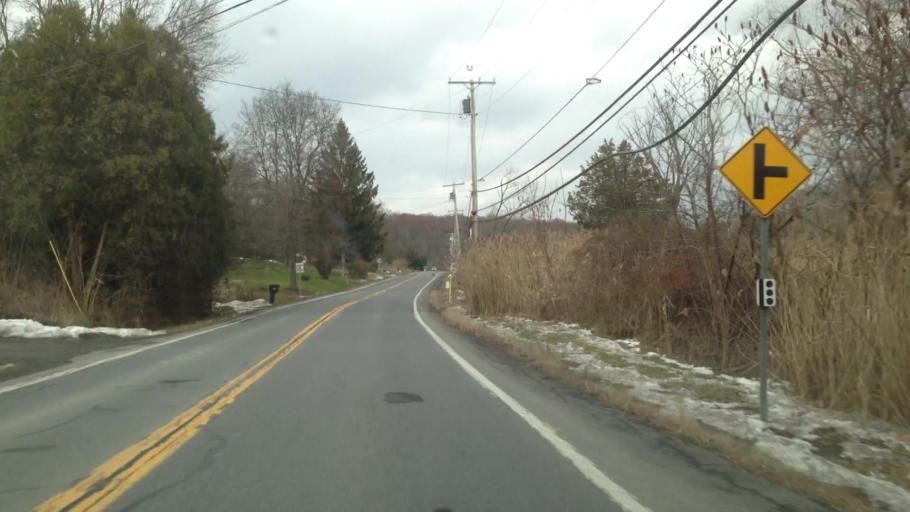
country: US
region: New York
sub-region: Ulster County
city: Lake Katrine
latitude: 41.9898
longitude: -73.9704
